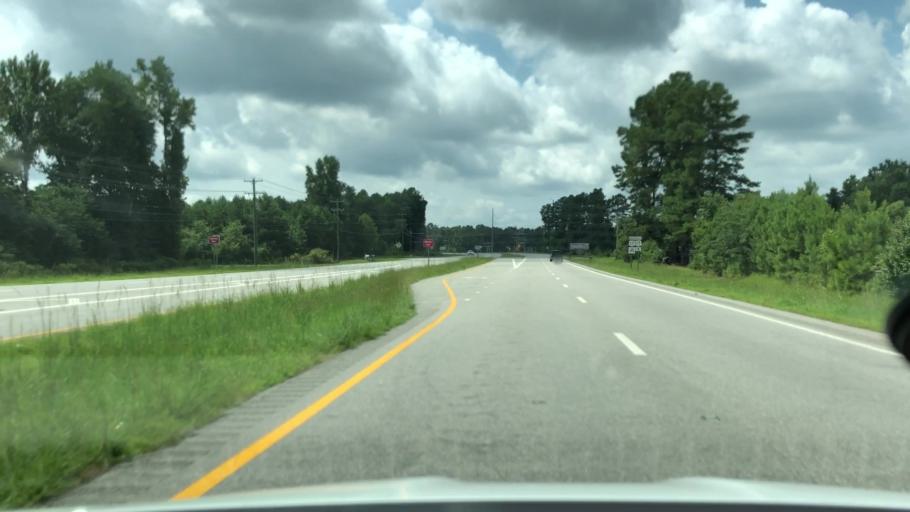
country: US
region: North Carolina
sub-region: Beaufort County
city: Washington
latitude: 35.4788
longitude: -77.1156
